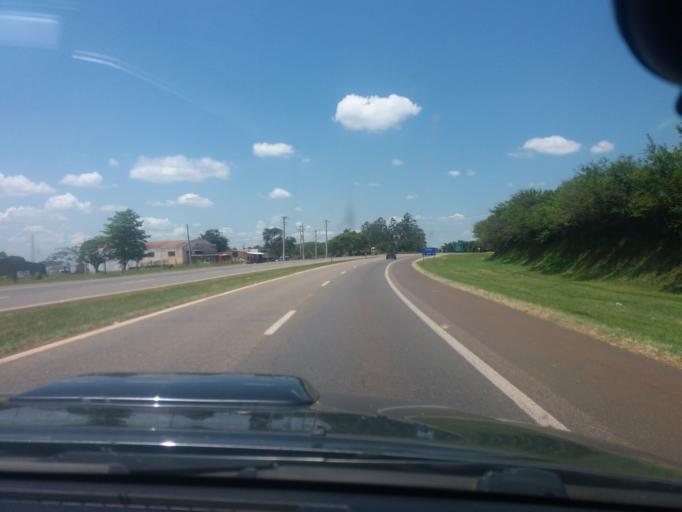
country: BR
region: Sao Paulo
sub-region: Tatui
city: Tatui
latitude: -23.3567
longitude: -47.8813
